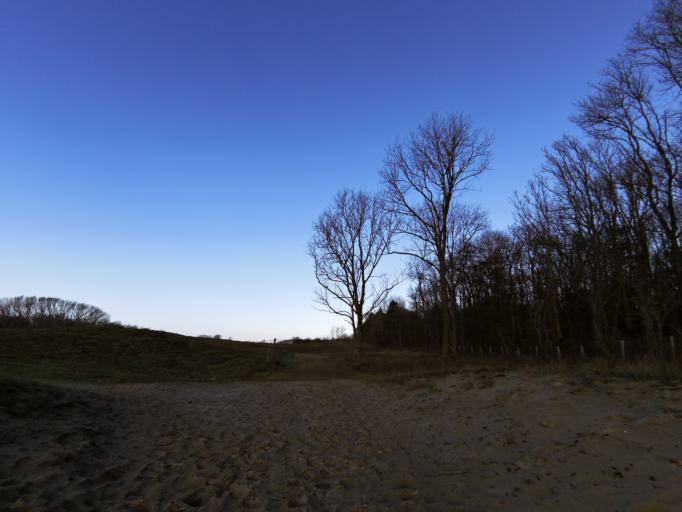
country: NL
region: South Holland
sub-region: Gemeente Goeree-Overflakkee
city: Goedereede
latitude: 51.8870
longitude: 4.0441
